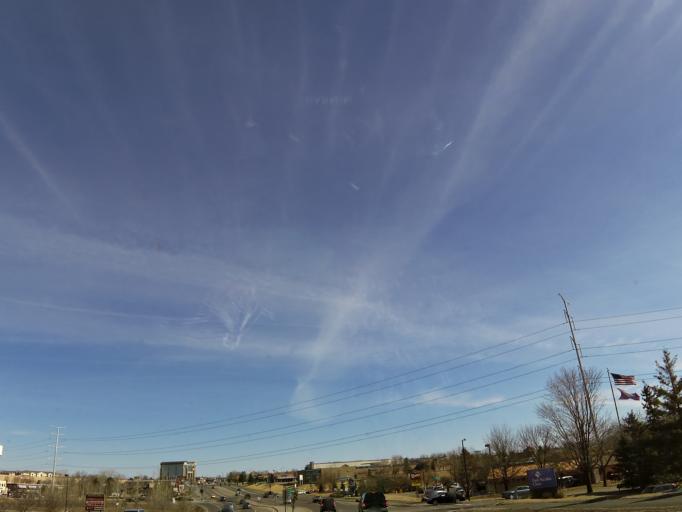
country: US
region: Minnesota
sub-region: Hennepin County
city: Eden Prairie
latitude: 44.8506
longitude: -93.4345
